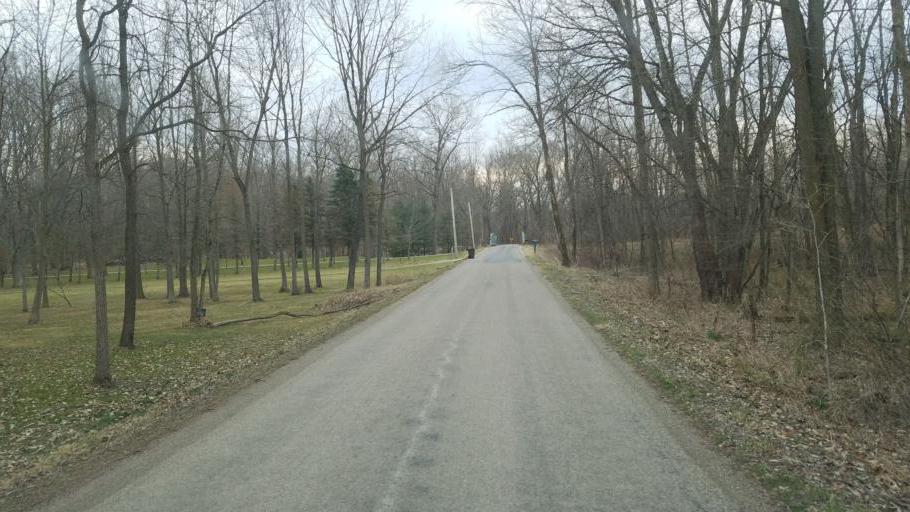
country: US
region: Ohio
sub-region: Richland County
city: Lincoln Heights
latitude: 40.7346
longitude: -82.3668
